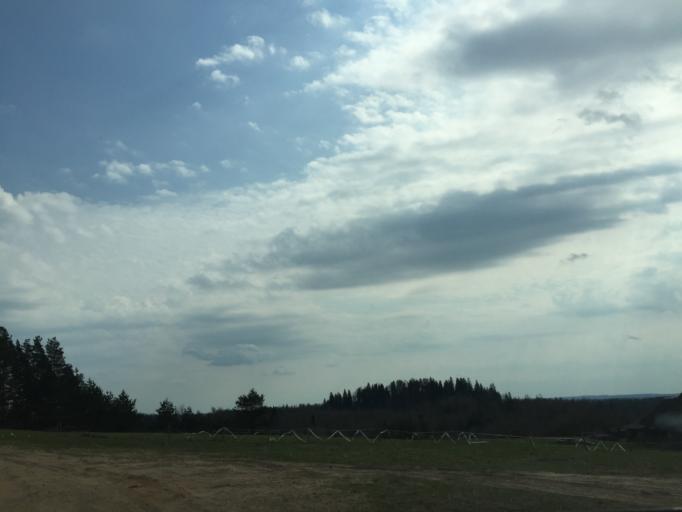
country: LV
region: Aluksnes Rajons
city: Aluksne
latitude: 57.5491
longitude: 26.9000
